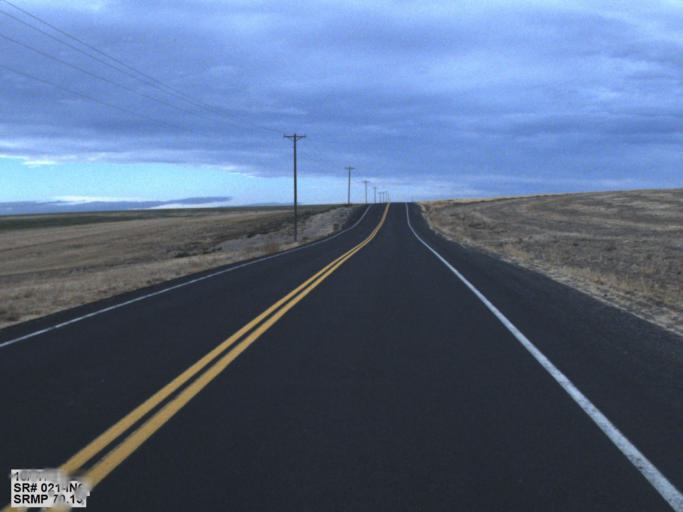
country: US
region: Washington
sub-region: Okanogan County
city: Coulee Dam
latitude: 47.4974
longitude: -118.7849
